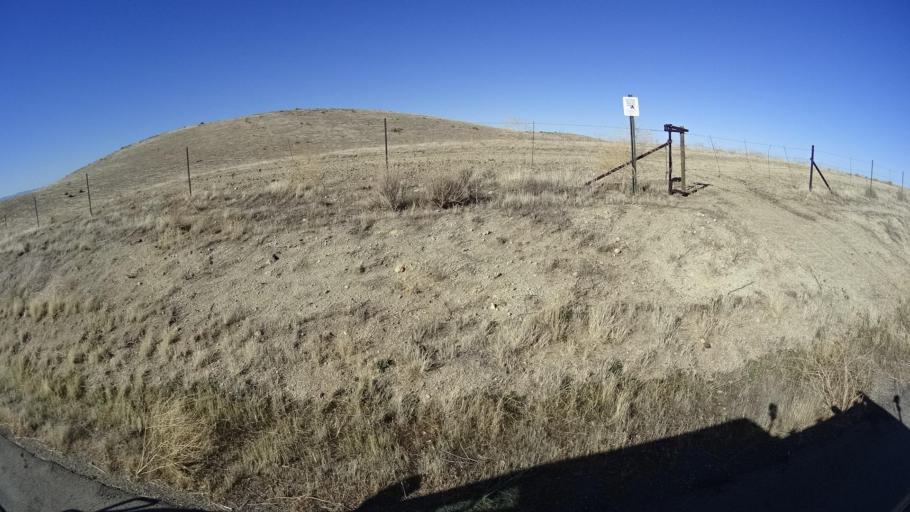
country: US
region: California
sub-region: Kern County
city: Maricopa
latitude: 34.9415
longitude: -119.4058
